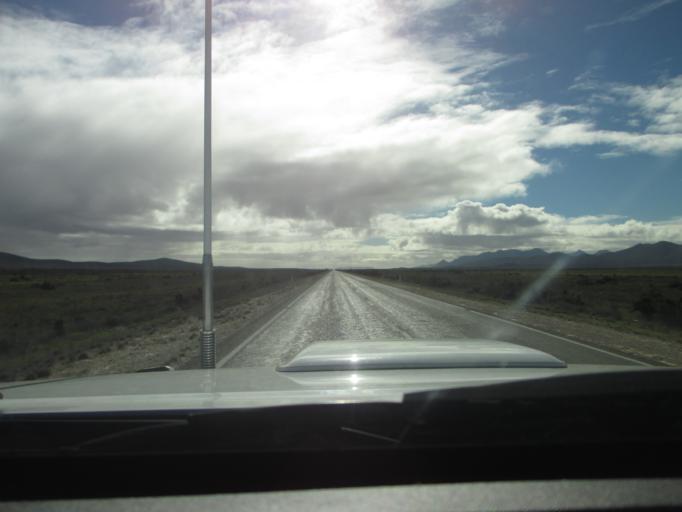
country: AU
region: South Australia
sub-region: Flinders Ranges
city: Quorn
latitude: -31.6786
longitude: 138.3670
